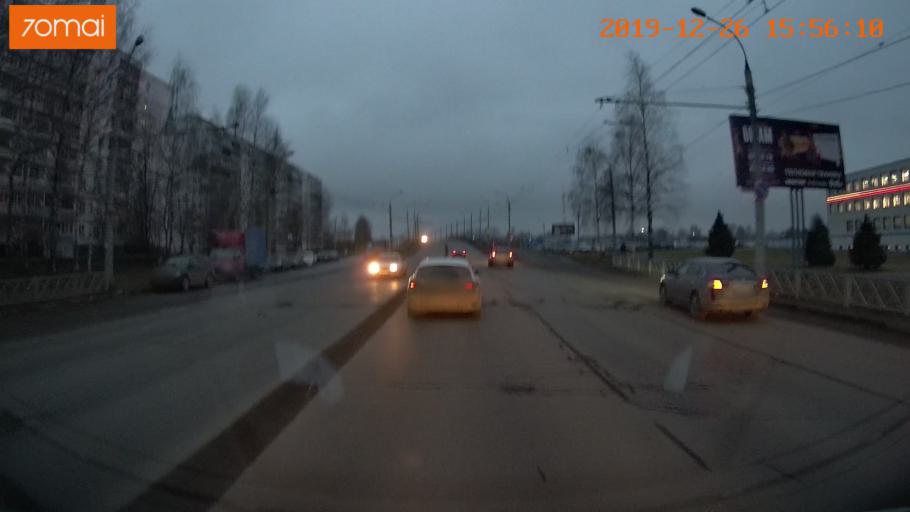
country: RU
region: Jaroslavl
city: Rybinsk
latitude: 58.0431
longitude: 38.8066
